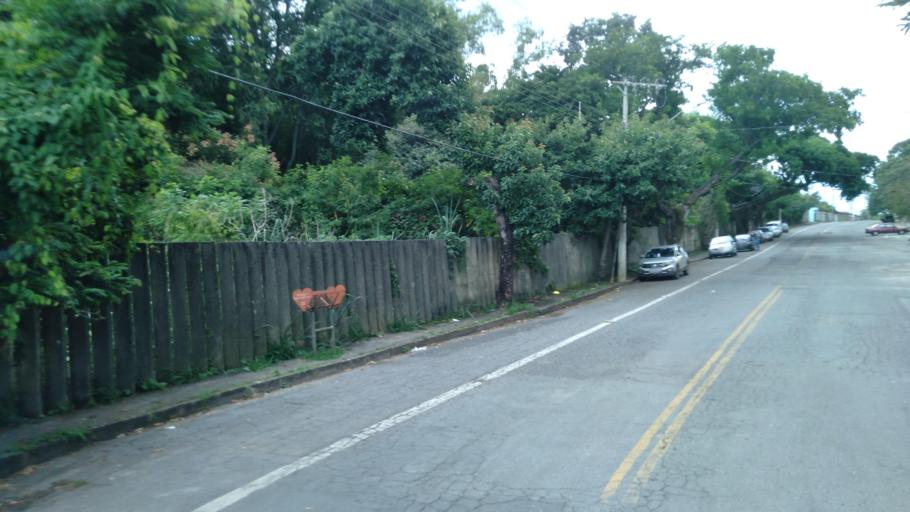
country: BR
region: Minas Gerais
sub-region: Contagem
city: Contagem
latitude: -19.9190
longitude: -44.0134
